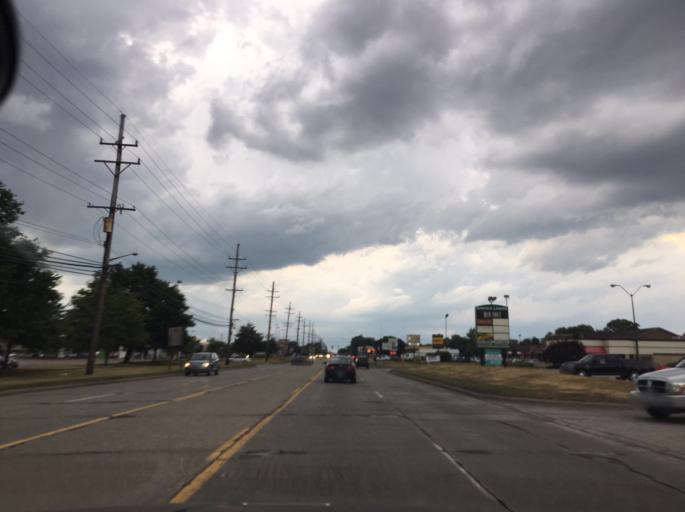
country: US
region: Michigan
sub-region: Macomb County
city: Clinton
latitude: 42.6022
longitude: -82.9525
